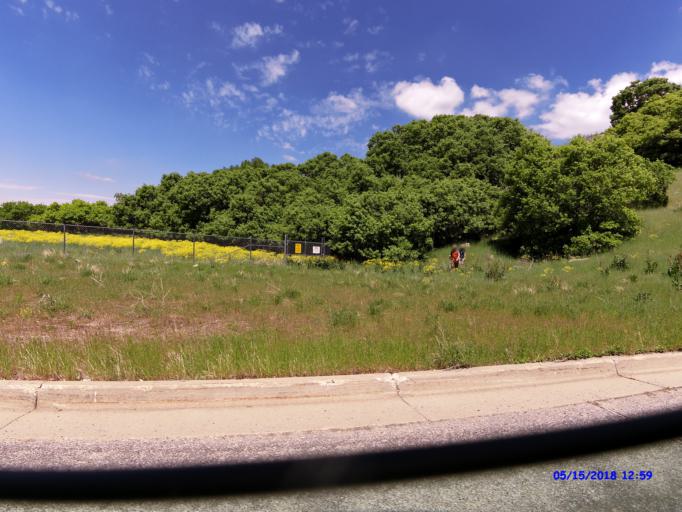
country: US
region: Utah
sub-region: Weber County
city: Uintah
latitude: 41.1635
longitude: -111.9232
